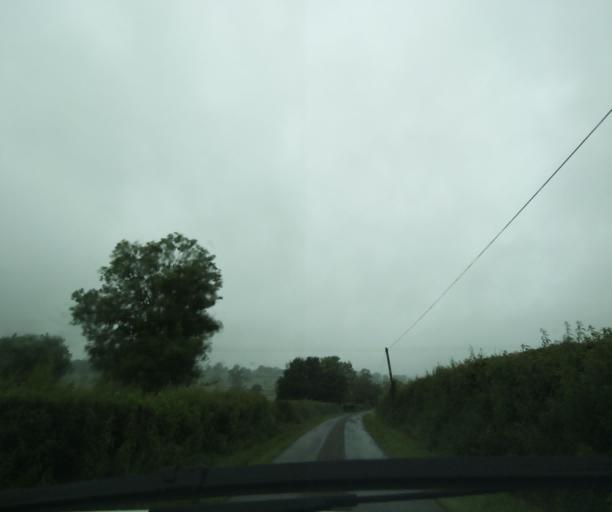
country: FR
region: Bourgogne
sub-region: Departement de Saone-et-Loire
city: Charolles
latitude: 46.4003
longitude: 4.2478
